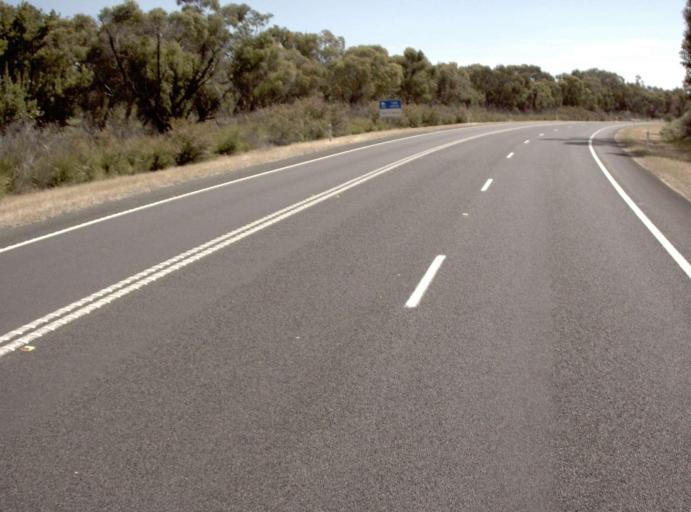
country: AU
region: Victoria
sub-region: Wellington
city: Sale
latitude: -37.9198
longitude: 147.2844
